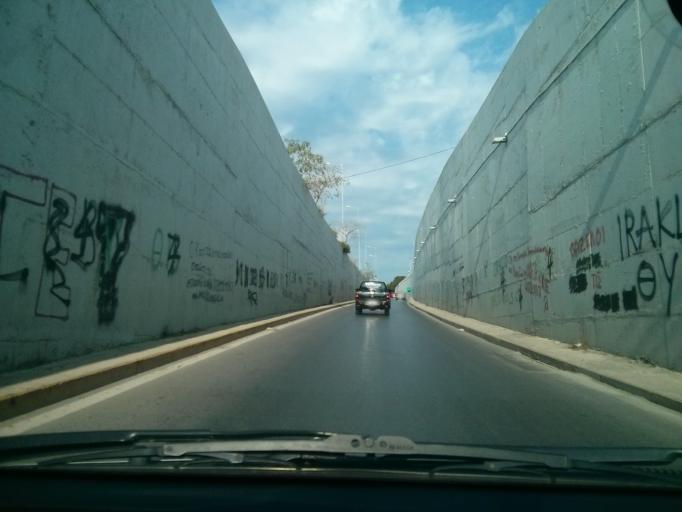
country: GR
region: Crete
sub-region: Nomos Irakleiou
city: Irakleion
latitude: 35.3205
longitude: 25.1443
